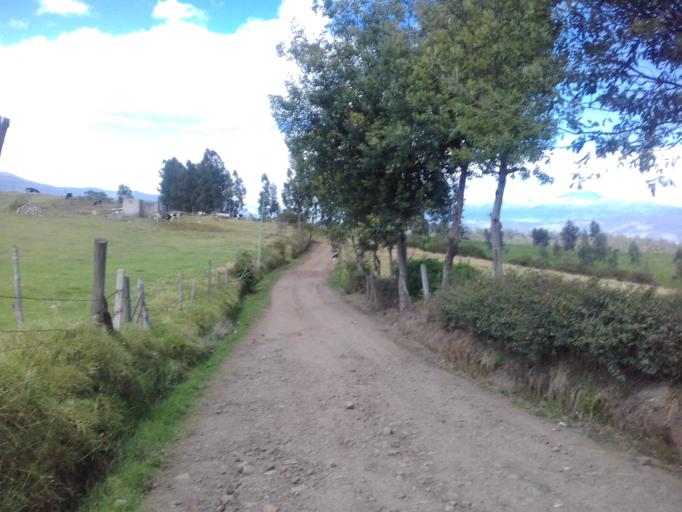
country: EC
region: Pichincha
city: Sangolqui
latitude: -0.3511
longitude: -78.4047
